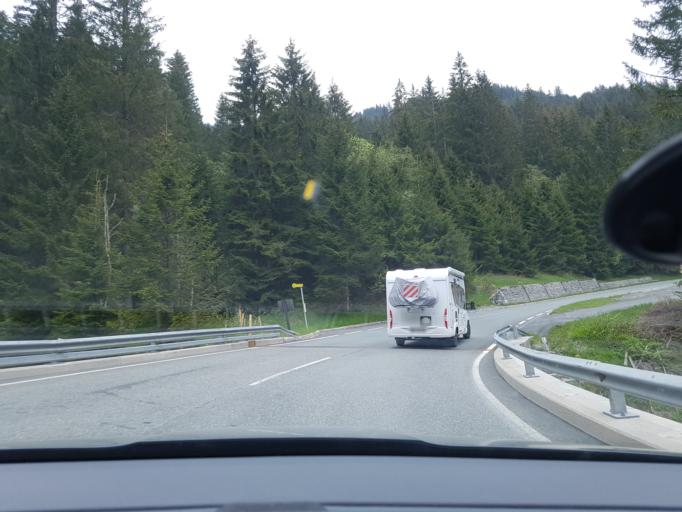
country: AT
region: Salzburg
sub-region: Politischer Bezirk Zell am See
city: Krimml
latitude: 47.2187
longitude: 12.1576
